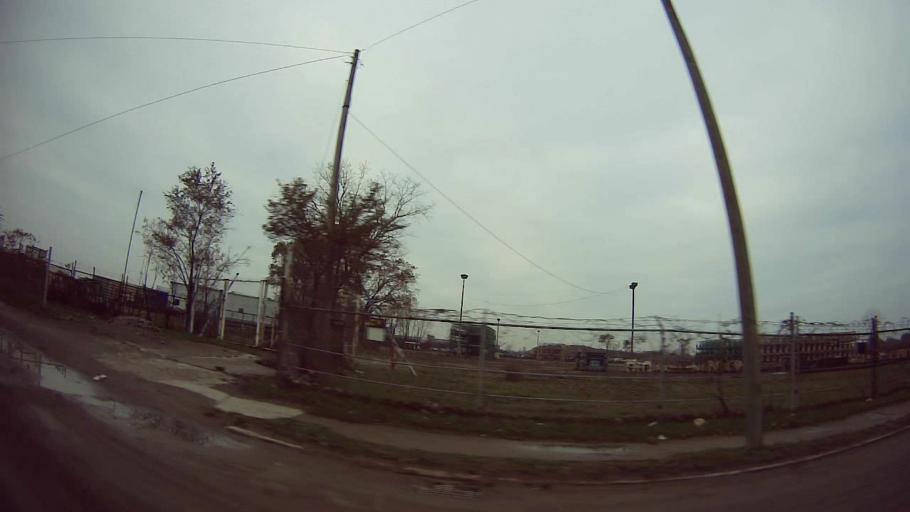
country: US
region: Michigan
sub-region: Wayne County
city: Highland Park
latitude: 42.4135
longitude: -83.0913
